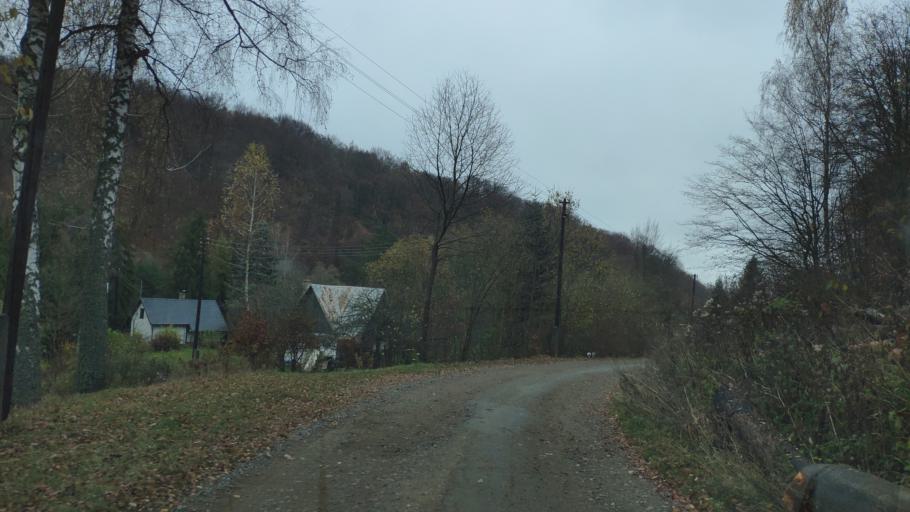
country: SK
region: Presovsky
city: Sabinov
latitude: 49.1376
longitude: 21.2165
